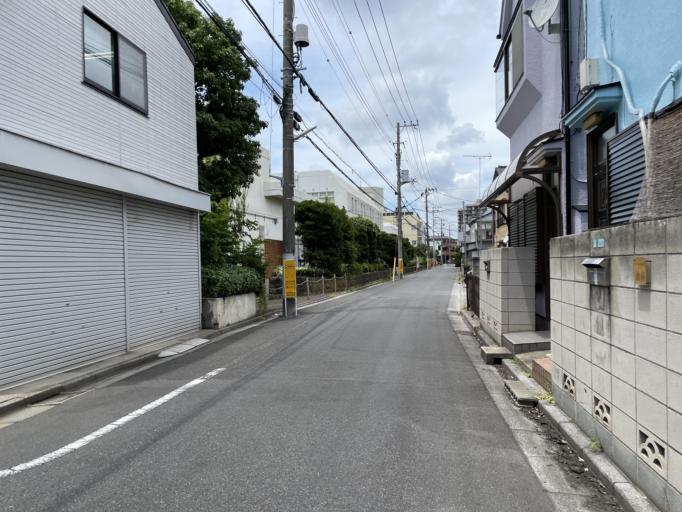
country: JP
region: Chiba
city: Matsudo
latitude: 35.7562
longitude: 139.8603
